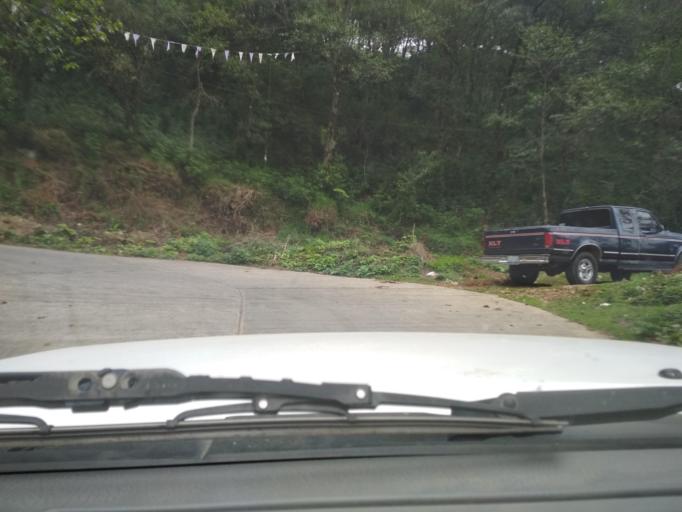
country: MX
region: Veracruz
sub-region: La Perla
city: Metlac Hernandez (Metlac Primero)
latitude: 18.9696
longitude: -97.1435
